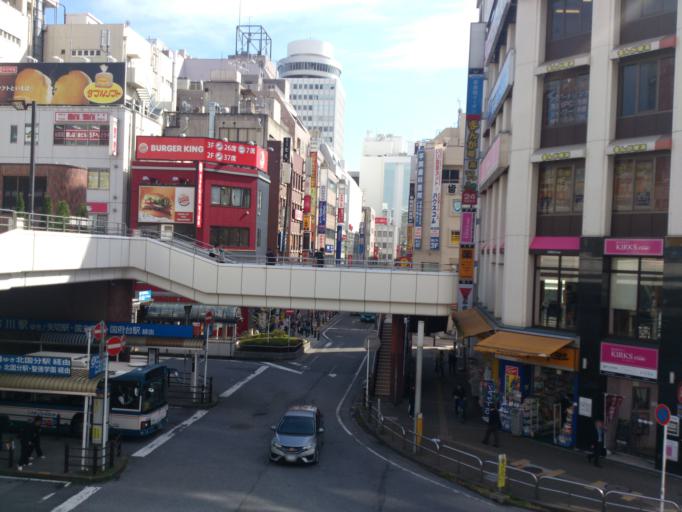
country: JP
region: Chiba
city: Matsudo
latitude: 35.7847
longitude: 139.8998
